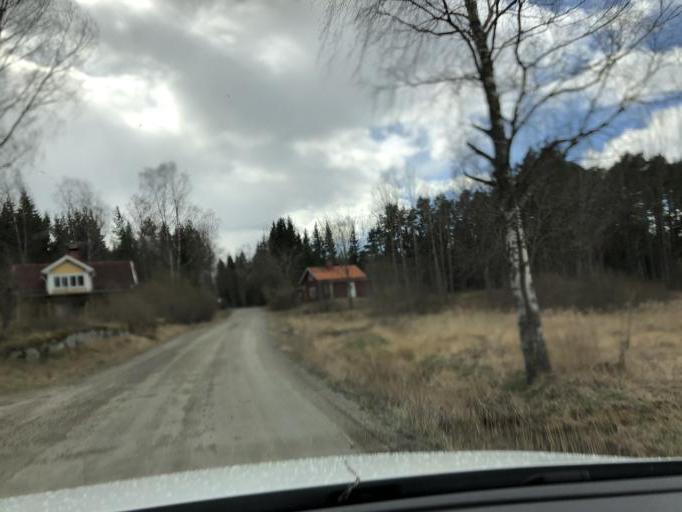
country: SE
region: Uppsala
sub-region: Heby Kommun
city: OEstervala
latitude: 60.3221
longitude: 17.1756
